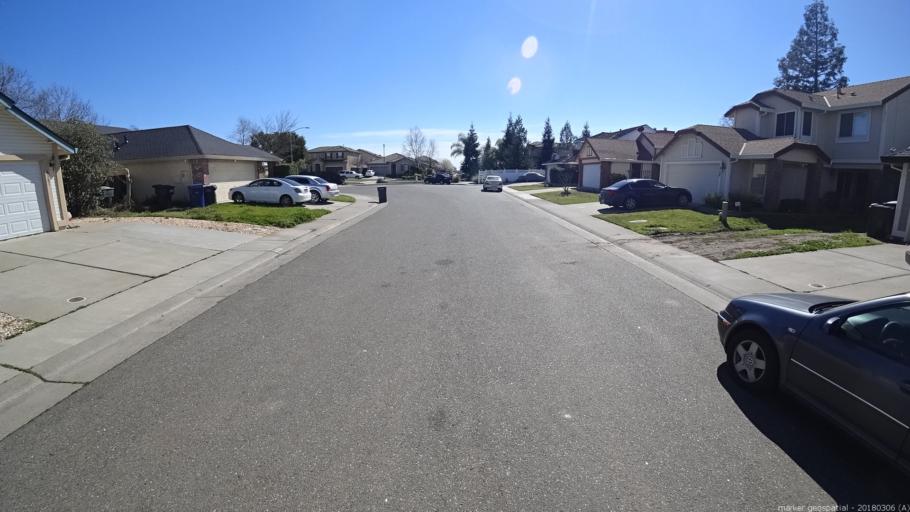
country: US
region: California
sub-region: Sacramento County
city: Vineyard
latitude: 38.4604
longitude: -121.3620
